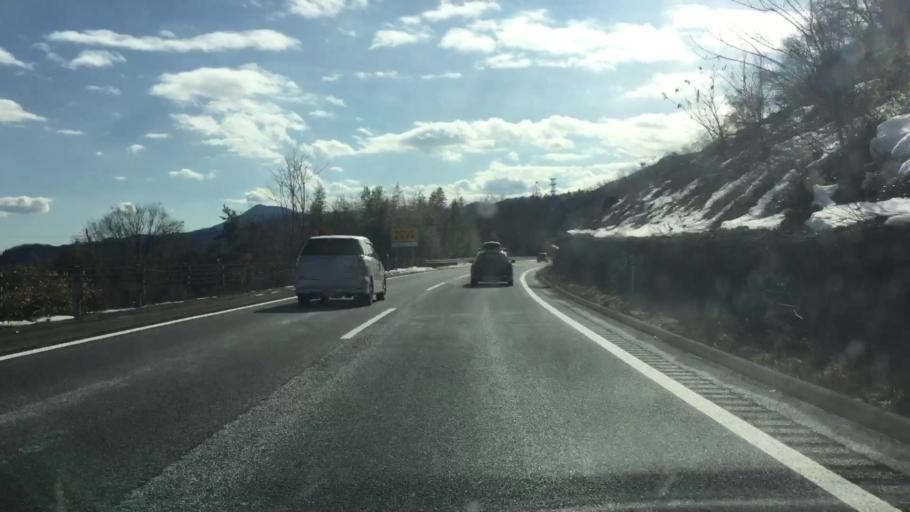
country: JP
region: Gunma
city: Numata
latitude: 36.7194
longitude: 138.9764
